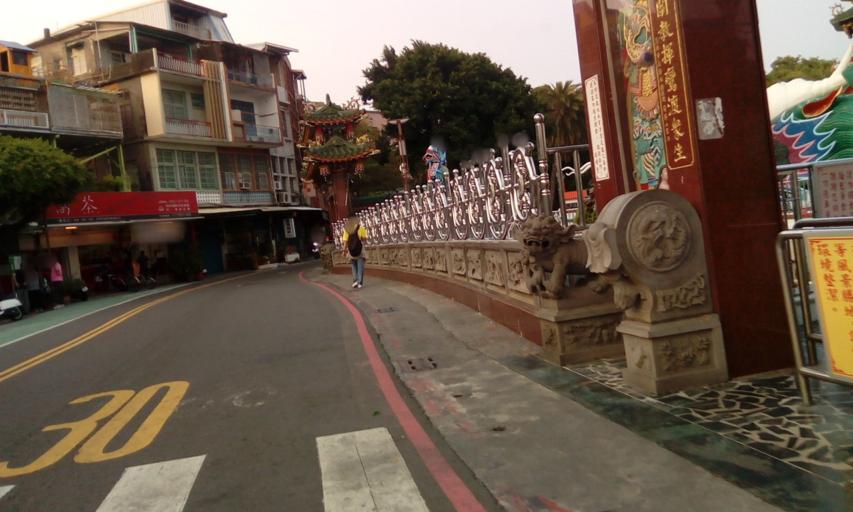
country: TW
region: Kaohsiung
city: Kaohsiung
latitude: 22.6821
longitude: 120.2924
